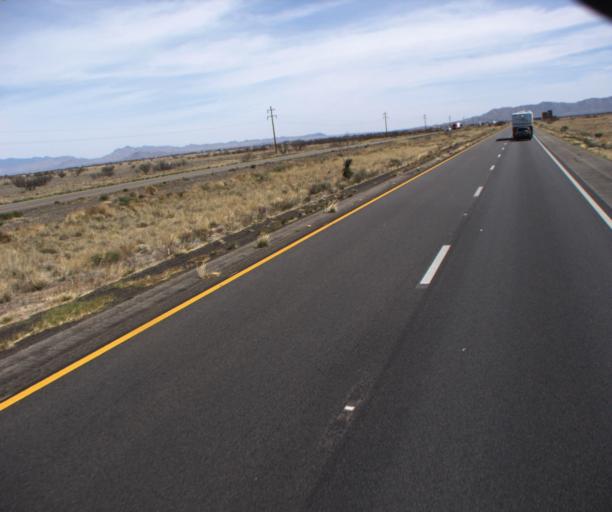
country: US
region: Arizona
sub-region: Cochise County
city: Willcox
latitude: 32.2047
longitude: -109.9018
